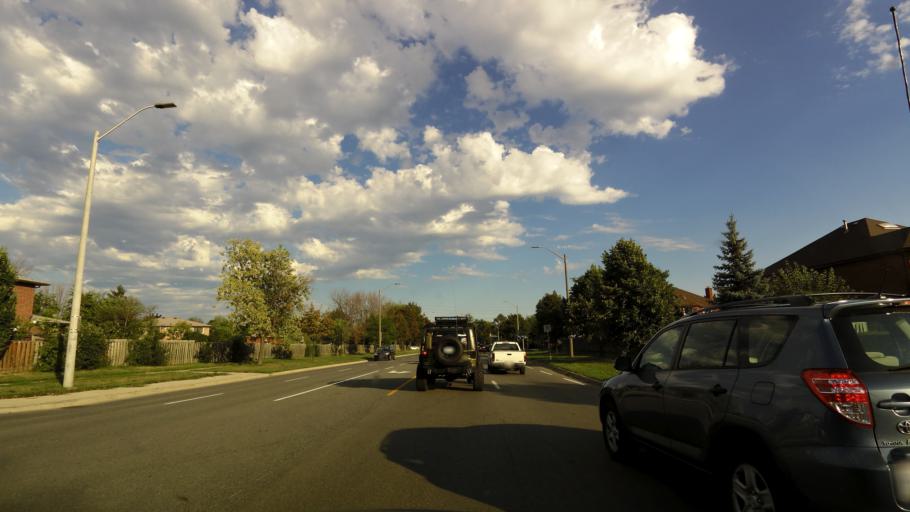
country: CA
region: Ontario
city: Mississauga
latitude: 43.5620
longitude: -79.6242
